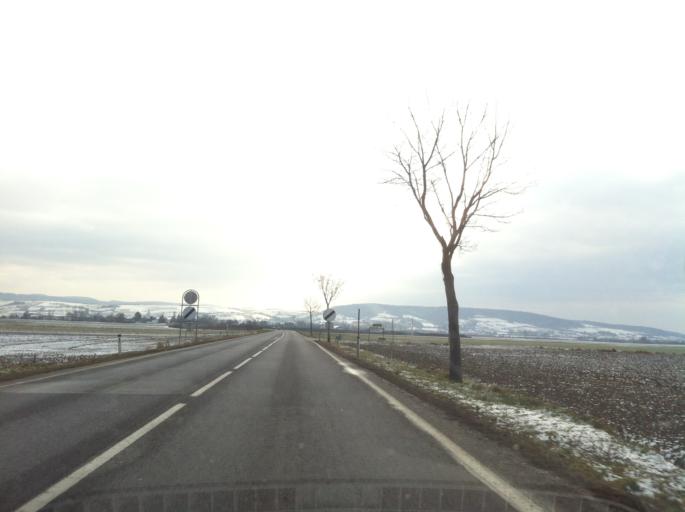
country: AT
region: Lower Austria
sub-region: Politischer Bezirk Tulln
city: Tulln
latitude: 48.3135
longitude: 16.0566
